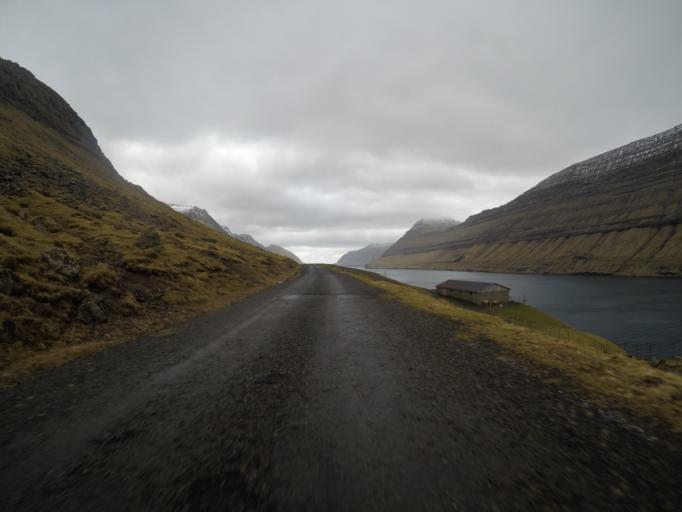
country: FO
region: Nordoyar
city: Klaksvik
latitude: 62.3051
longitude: -6.5390
